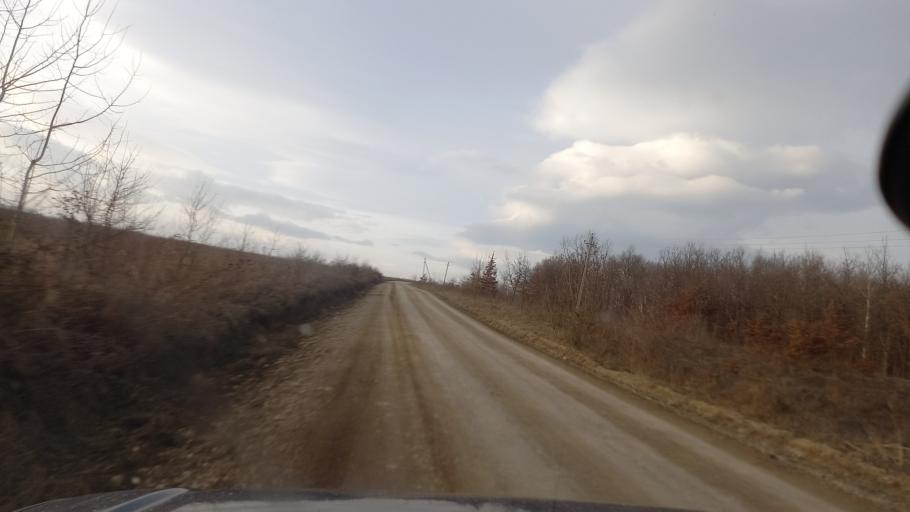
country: RU
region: Adygeya
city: Kamennomostskiy
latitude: 44.1947
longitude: 40.2549
